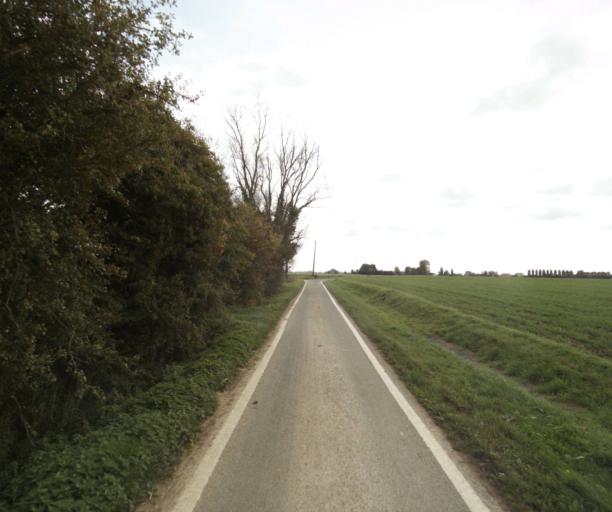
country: FR
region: Nord-Pas-de-Calais
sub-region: Departement du Pas-de-Calais
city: Fleurbaix
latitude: 50.6610
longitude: 2.8425
